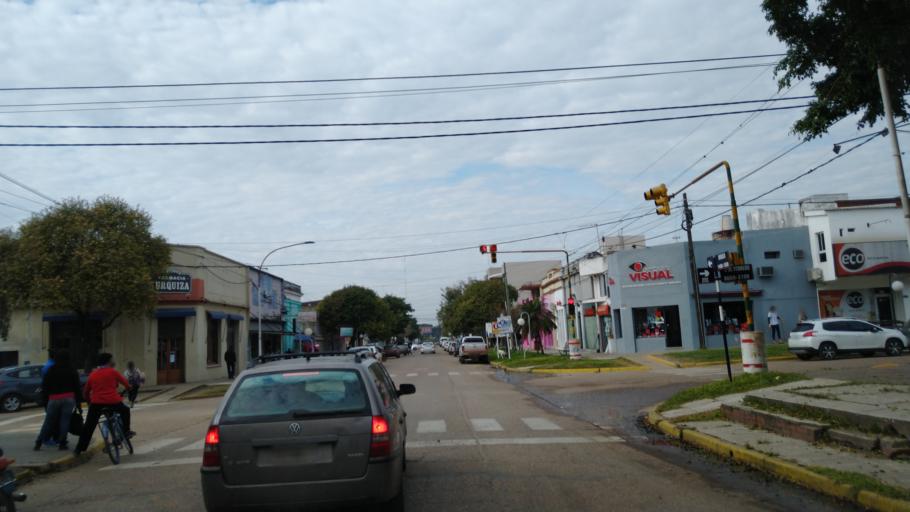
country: AR
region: Entre Rios
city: Chajari
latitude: -30.7590
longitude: -57.9847
